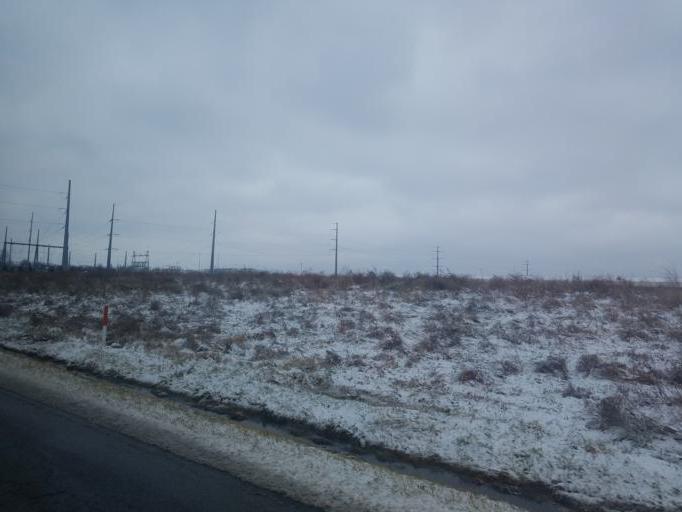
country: US
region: Ohio
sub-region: Franklin County
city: New Albany
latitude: 40.0971
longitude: -82.7524
